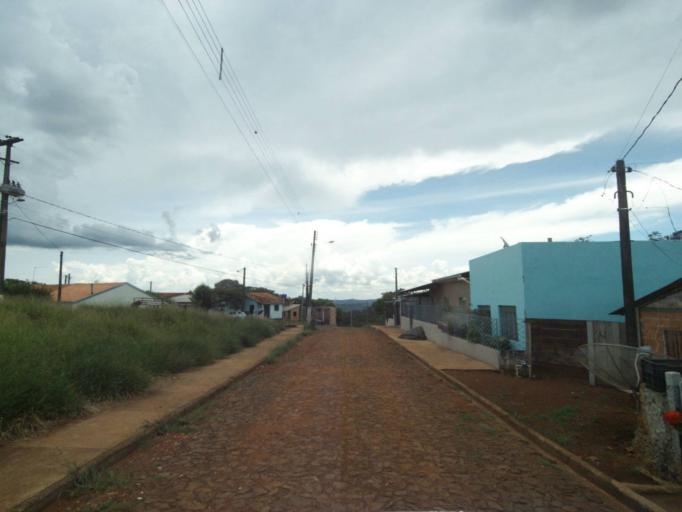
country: BR
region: Parana
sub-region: Guaraniacu
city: Guaraniacu
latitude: -25.1045
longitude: -52.8577
